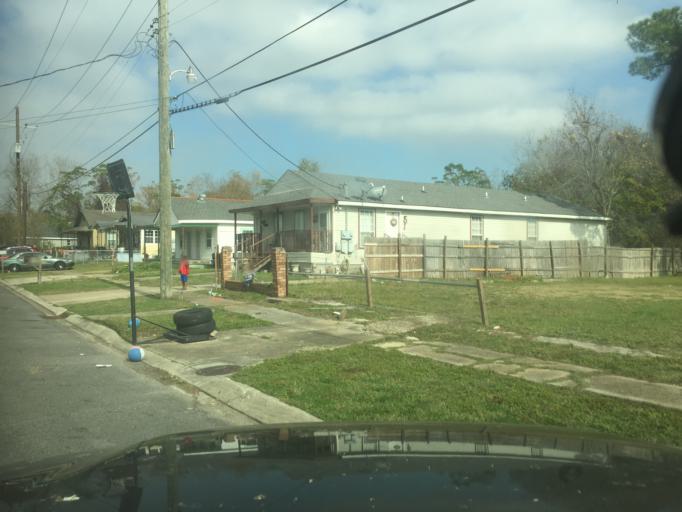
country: US
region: Louisiana
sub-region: Orleans Parish
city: New Orleans
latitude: 29.9967
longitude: -90.0408
